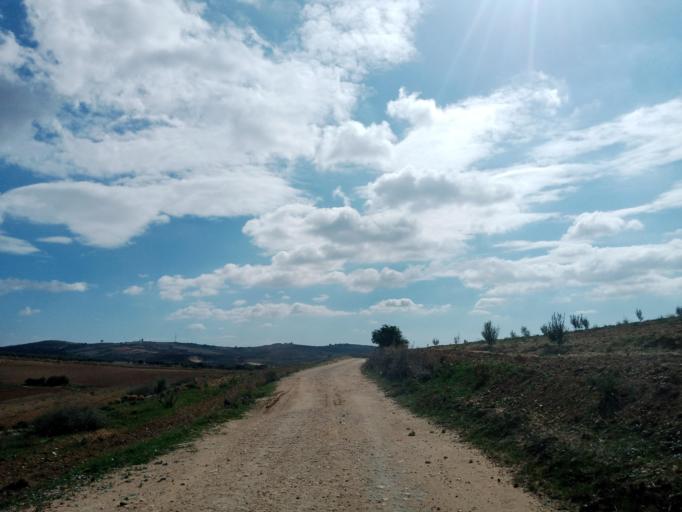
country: TN
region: Tunis
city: Oued Lill
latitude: 36.8087
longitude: 9.9843
